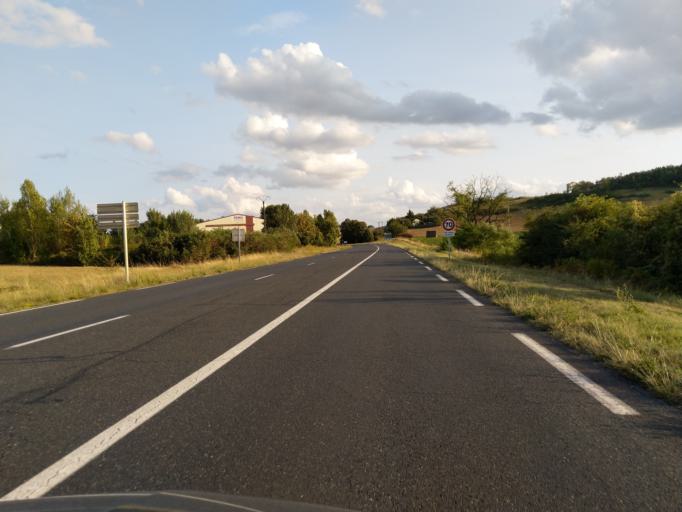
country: FR
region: Midi-Pyrenees
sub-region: Departement du Tarn
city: Realmont
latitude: 43.8047
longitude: 2.1828
